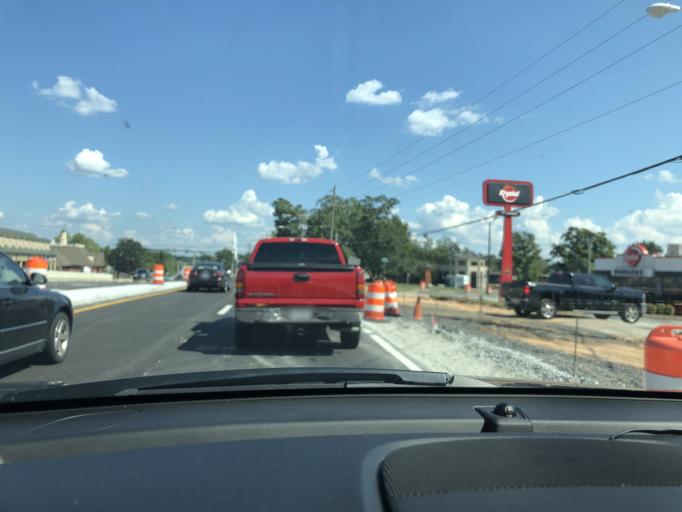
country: US
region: Georgia
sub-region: Gwinnett County
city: Snellville
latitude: 33.8571
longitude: -84.0182
